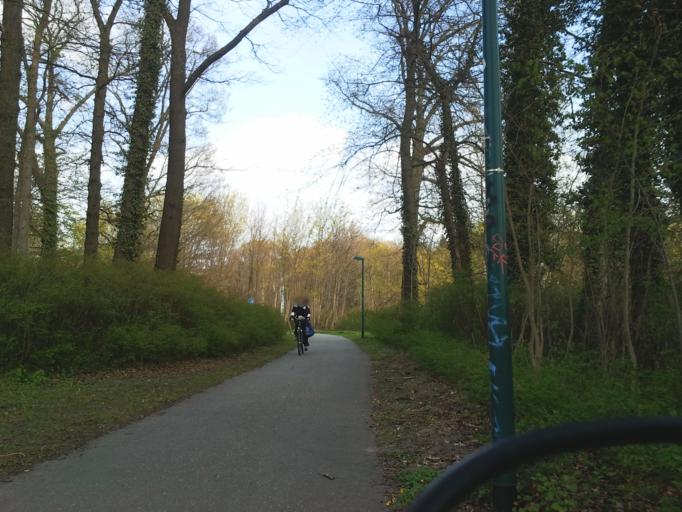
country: DE
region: Mecklenburg-Vorpommern
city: Rostock
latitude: 54.0807
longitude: 12.1641
